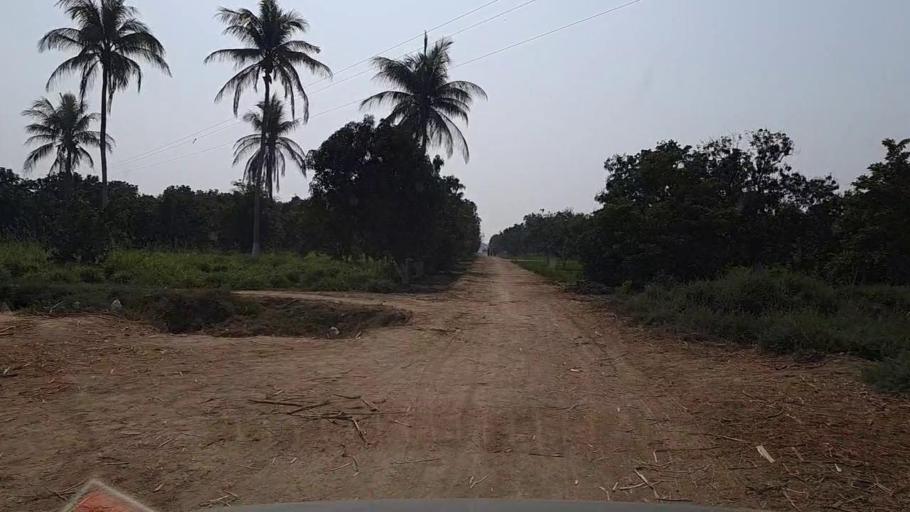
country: PK
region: Sindh
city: Mirwah Gorchani
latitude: 25.3343
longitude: 68.9926
